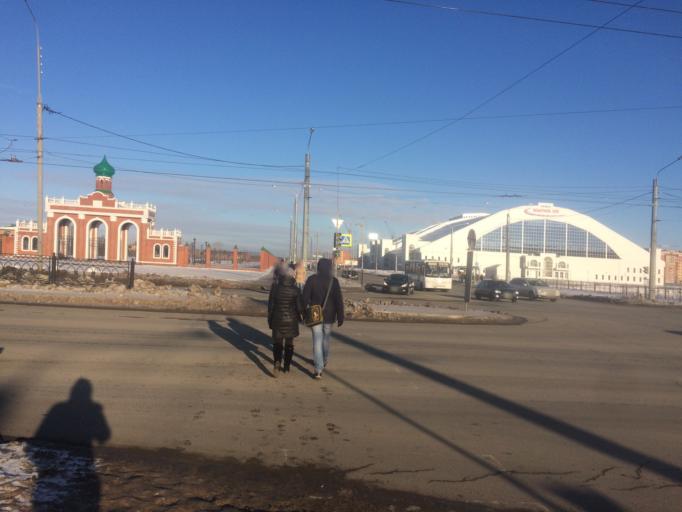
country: RU
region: Mariy-El
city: Yoshkar-Ola
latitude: 56.6371
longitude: 47.9125
